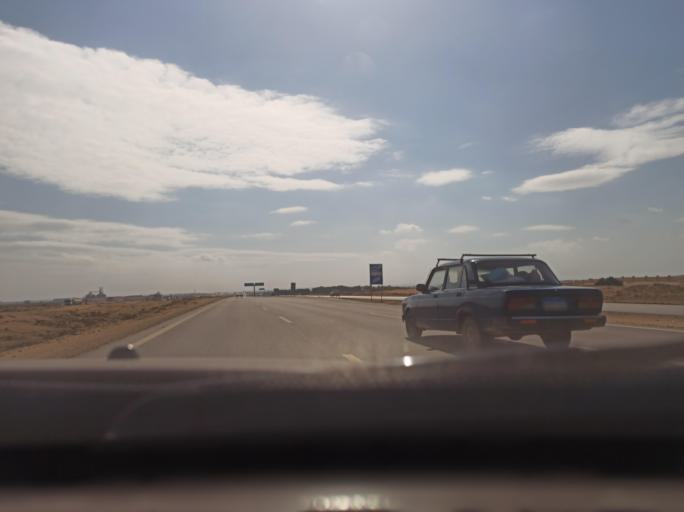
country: EG
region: Muhafazat al Fayyum
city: Tamiyah
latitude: 29.5571
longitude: 31.0598
